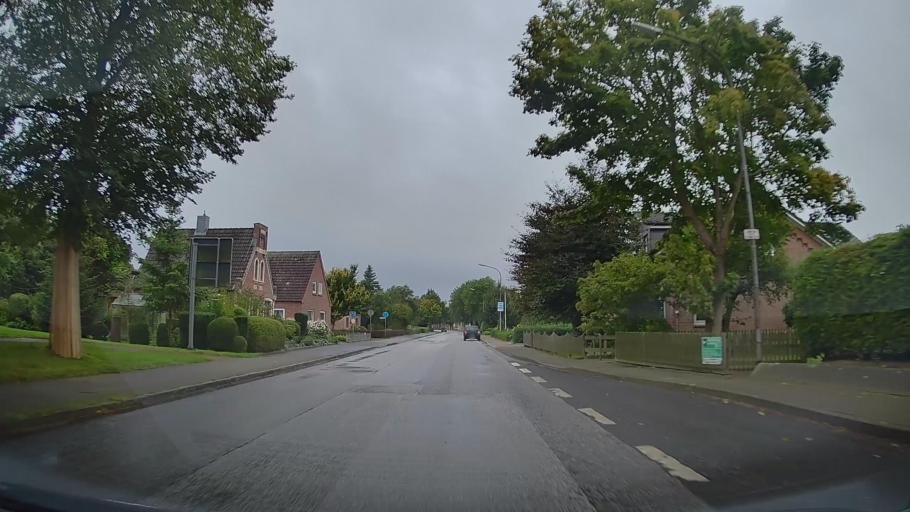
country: DE
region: Schleswig-Holstein
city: Brokdorf
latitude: 53.8618
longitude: 9.3293
